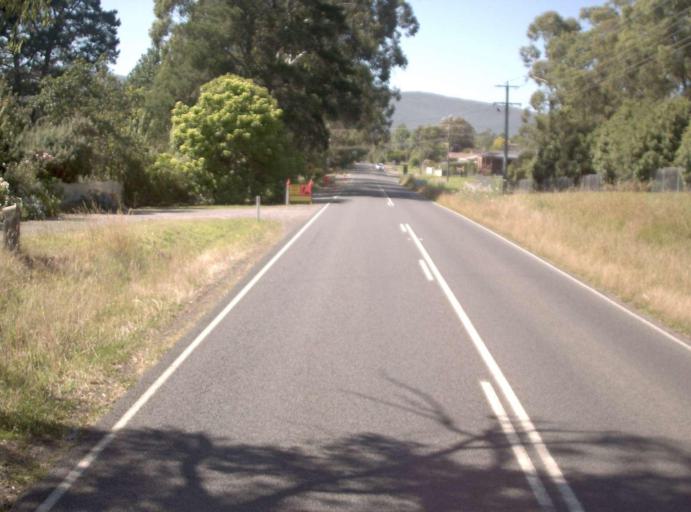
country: AU
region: Victoria
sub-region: Yarra Ranges
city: Healesville
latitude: -37.6598
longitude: 145.5296
